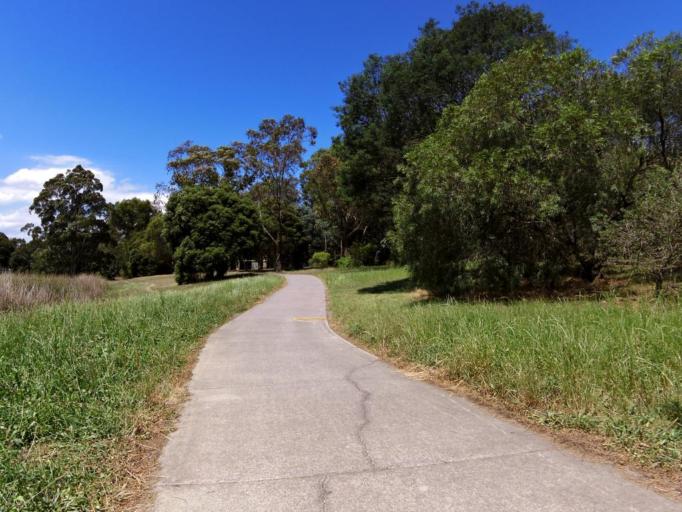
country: AU
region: Victoria
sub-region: Monash
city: Notting Hill
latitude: -37.8844
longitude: 145.1437
